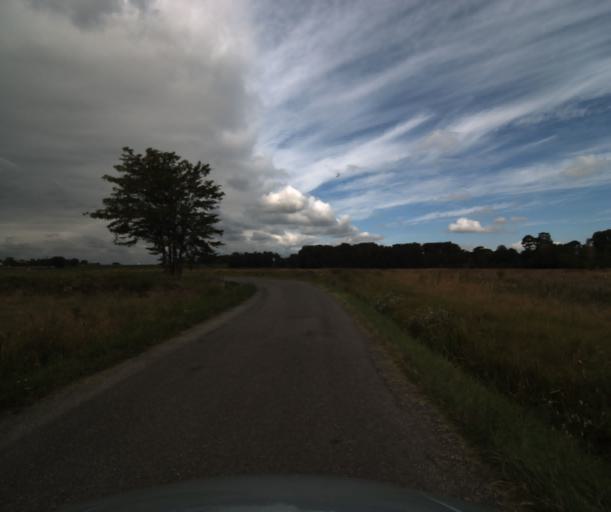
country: FR
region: Midi-Pyrenees
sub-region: Departement de la Haute-Garonne
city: Seysses
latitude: 43.4604
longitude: 1.3037
